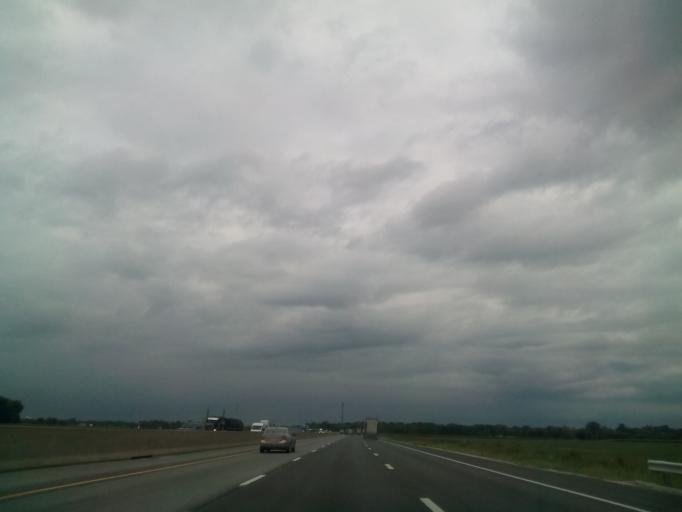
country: US
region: Ohio
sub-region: Sandusky County
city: Woodville
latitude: 41.4761
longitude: -83.3376
